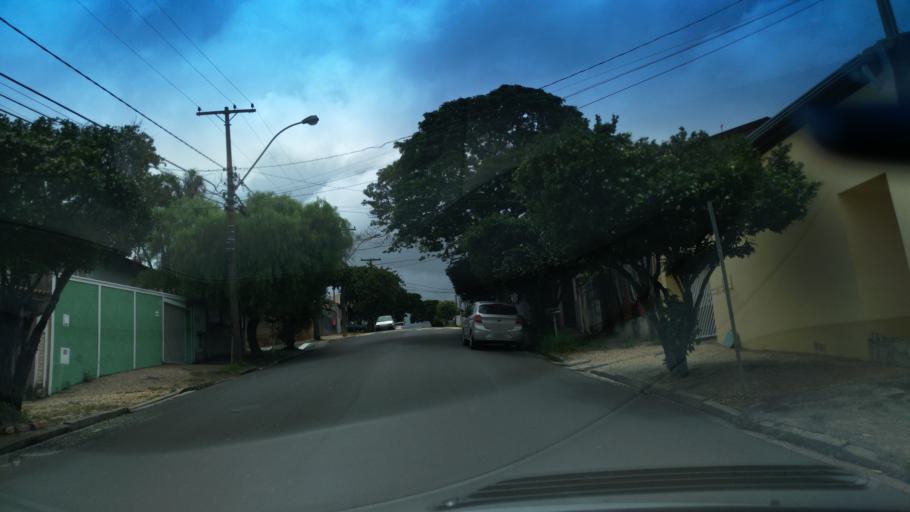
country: BR
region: Sao Paulo
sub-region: Valinhos
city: Valinhos
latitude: -22.9536
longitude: -46.9834
